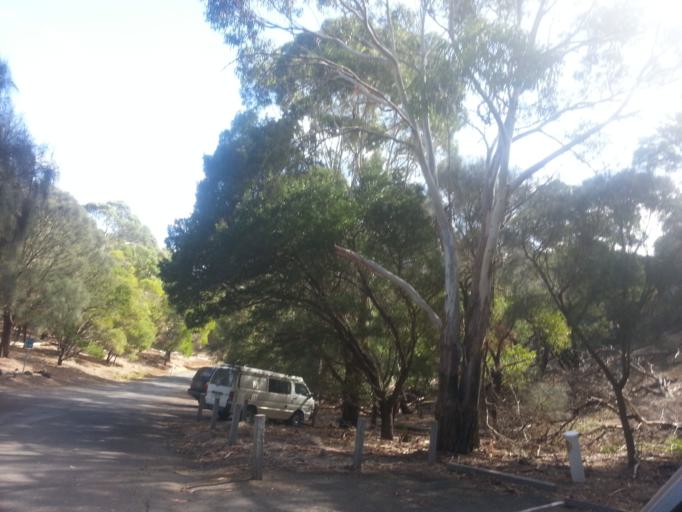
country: AU
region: Victoria
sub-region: Warrnambool
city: Warrnambool
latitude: -38.3206
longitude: 142.3636
